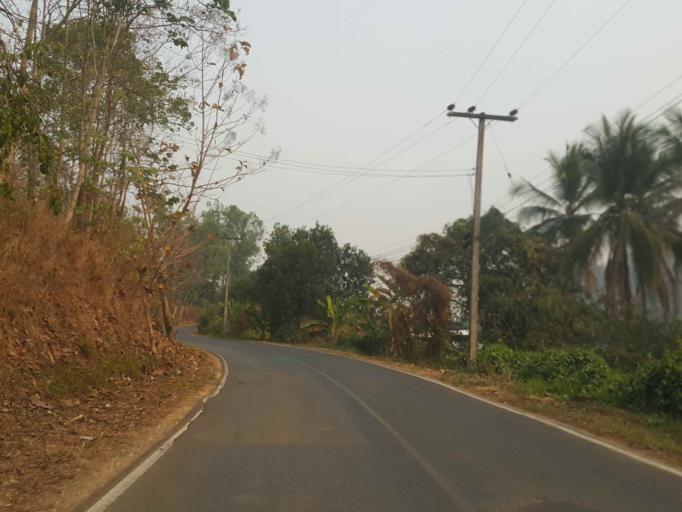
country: TH
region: Chiang Mai
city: Mae Taeng
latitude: 19.1244
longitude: 98.8867
